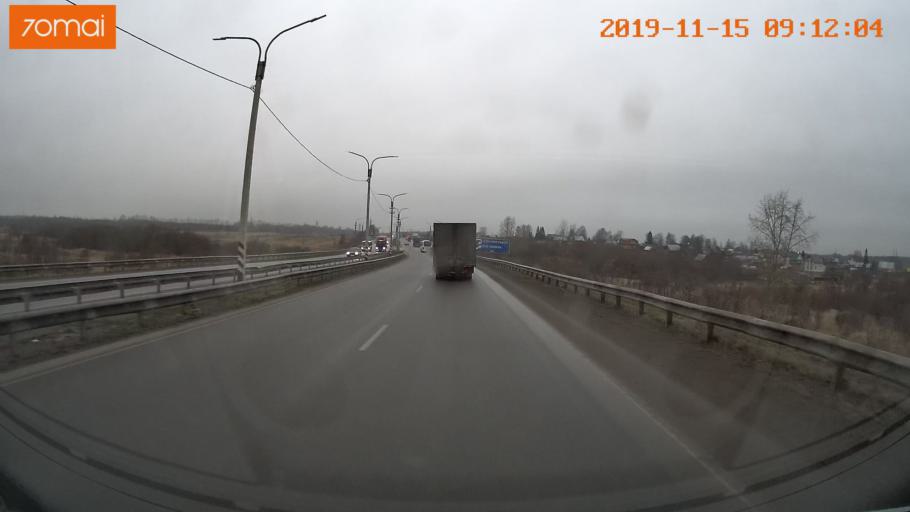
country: RU
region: Vologda
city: Tonshalovo
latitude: 59.2043
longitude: 37.9411
